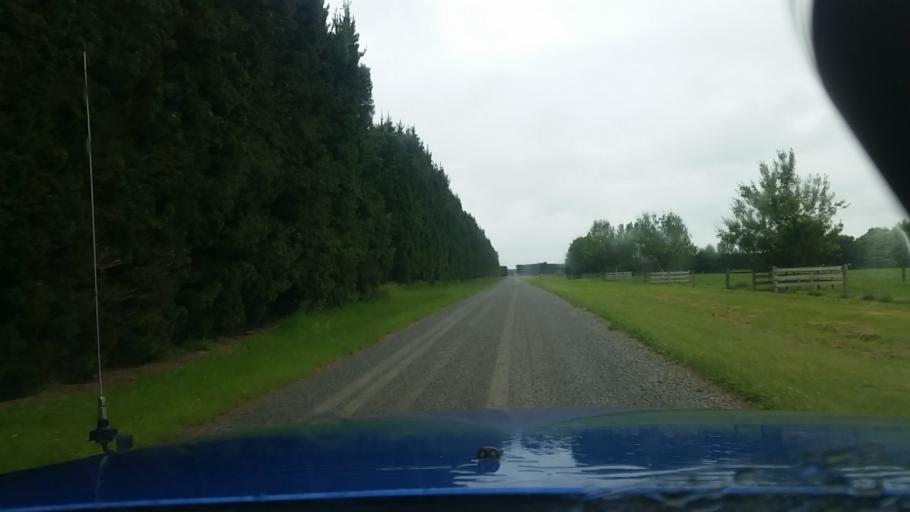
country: NZ
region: Canterbury
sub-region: Ashburton District
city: Tinwald
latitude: -43.9016
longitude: 171.5857
